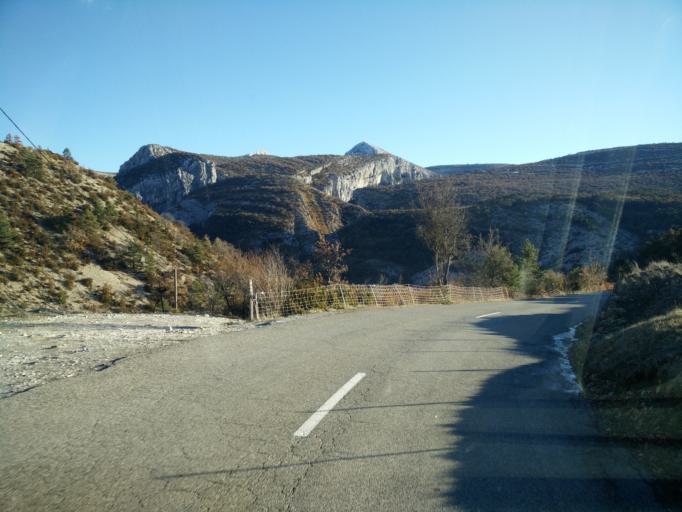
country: FR
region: Provence-Alpes-Cote d'Azur
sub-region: Departement des Alpes-de-Haute-Provence
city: Castellane
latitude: 43.7945
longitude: 6.3838
